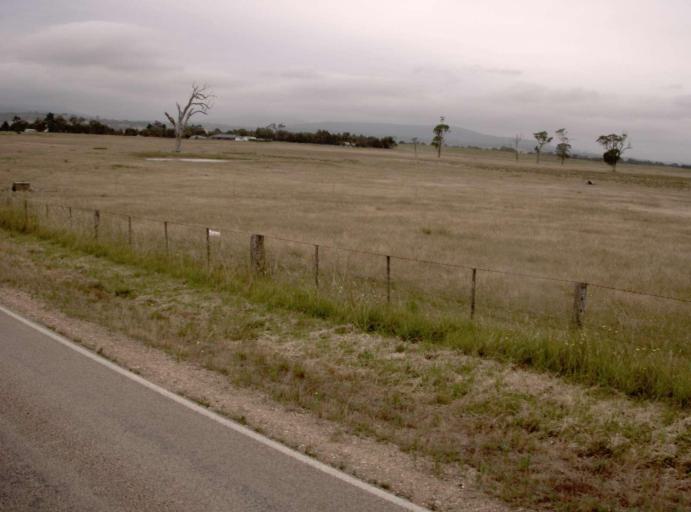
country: AU
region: Victoria
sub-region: East Gippsland
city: Bairnsdale
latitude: -37.8087
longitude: 147.4379
